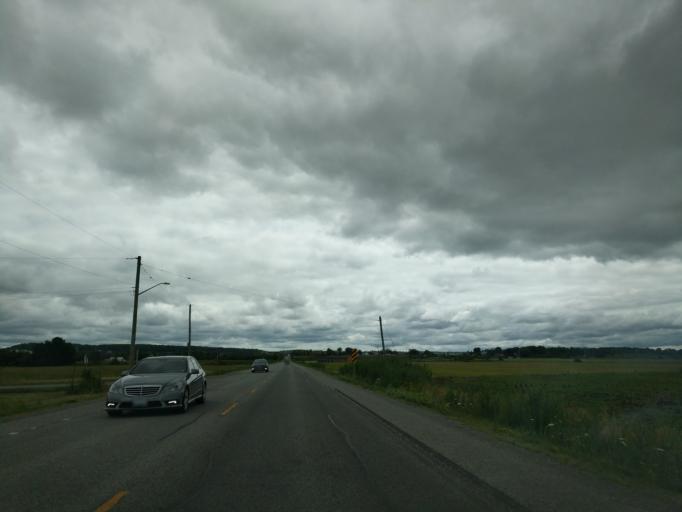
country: CA
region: Ontario
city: Thorold
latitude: 43.1729
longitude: -79.1687
